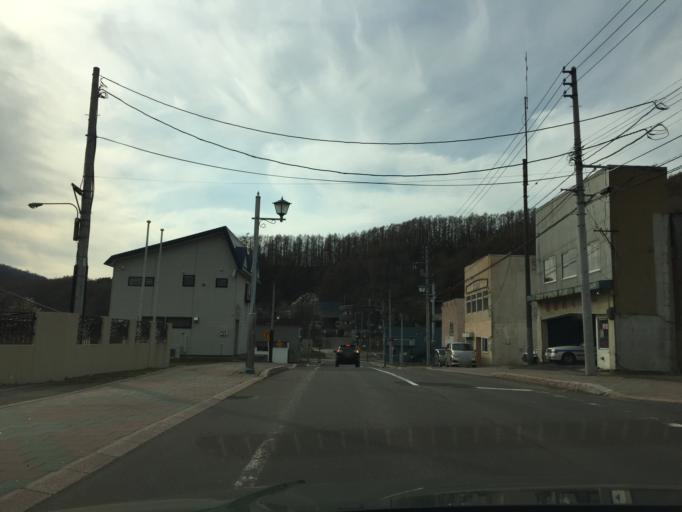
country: JP
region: Hokkaido
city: Utashinai
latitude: 43.5221
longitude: 142.0408
